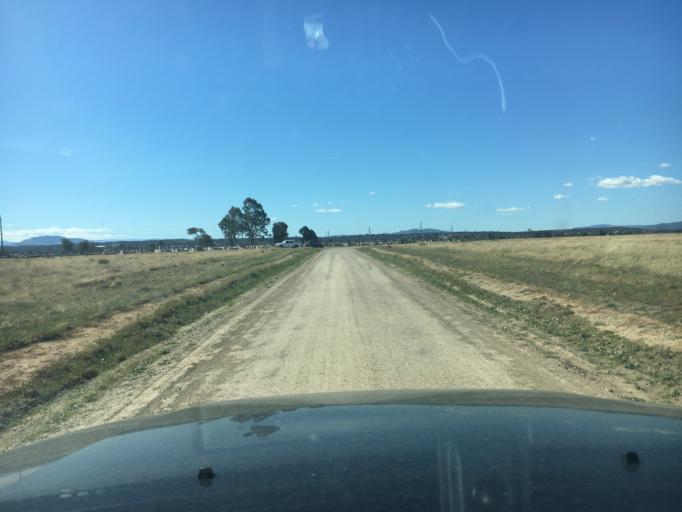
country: AU
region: New South Wales
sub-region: Singleton
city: Singleton
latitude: -32.5913
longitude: 151.1802
